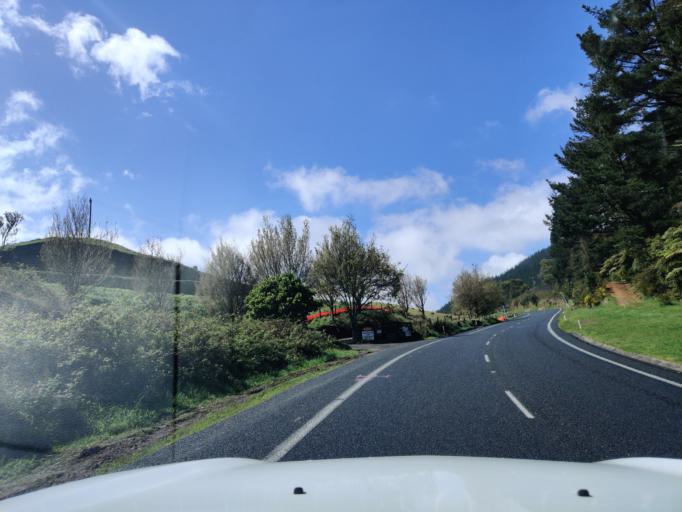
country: NZ
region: Bay of Plenty
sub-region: Rotorua District
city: Rotorua
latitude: -38.1585
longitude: 176.2972
